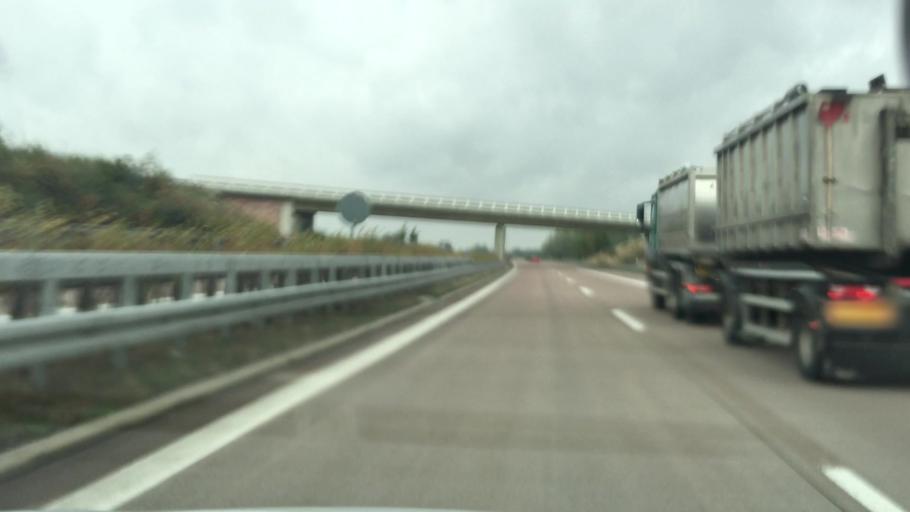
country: DE
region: Saxony
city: Penig
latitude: 50.9445
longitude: 12.6893
